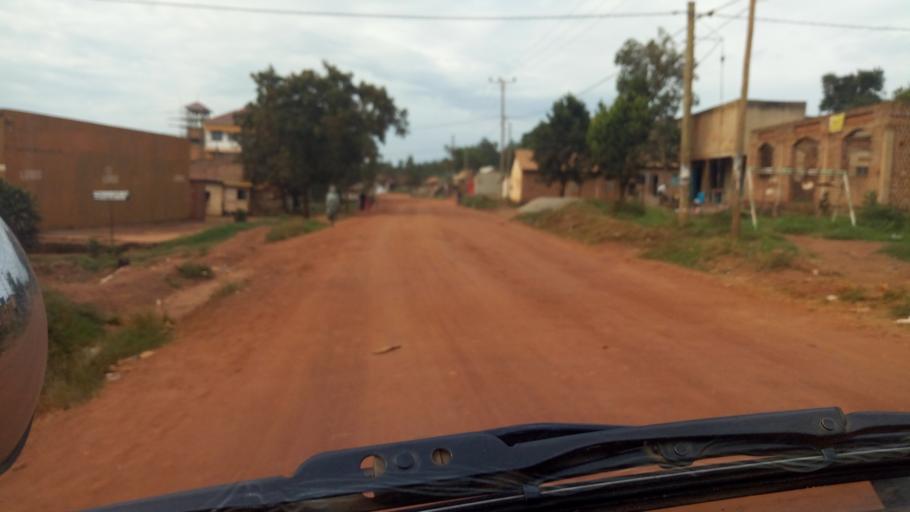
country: UG
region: Central Region
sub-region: Wakiso District
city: Bweyogerere
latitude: 0.3581
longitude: 32.7013
